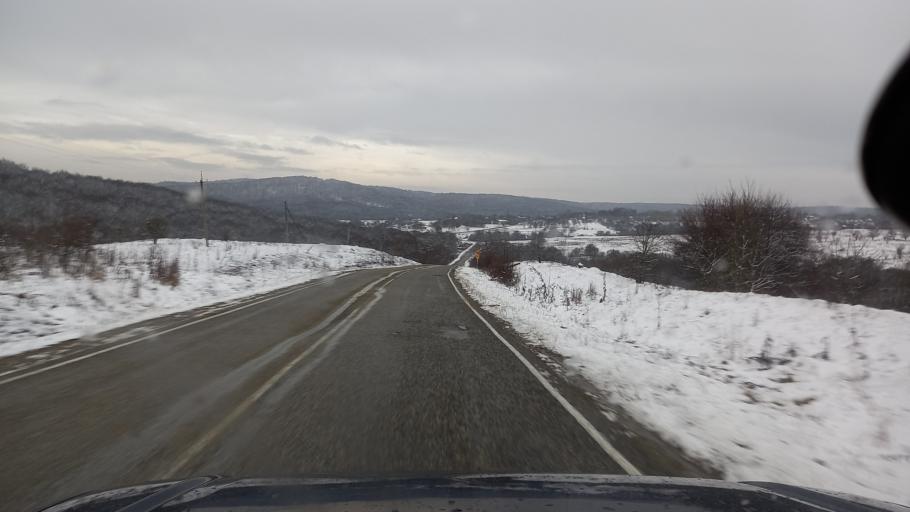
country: RU
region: Adygeya
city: Abadzekhskaya
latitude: 44.3593
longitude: 40.3927
